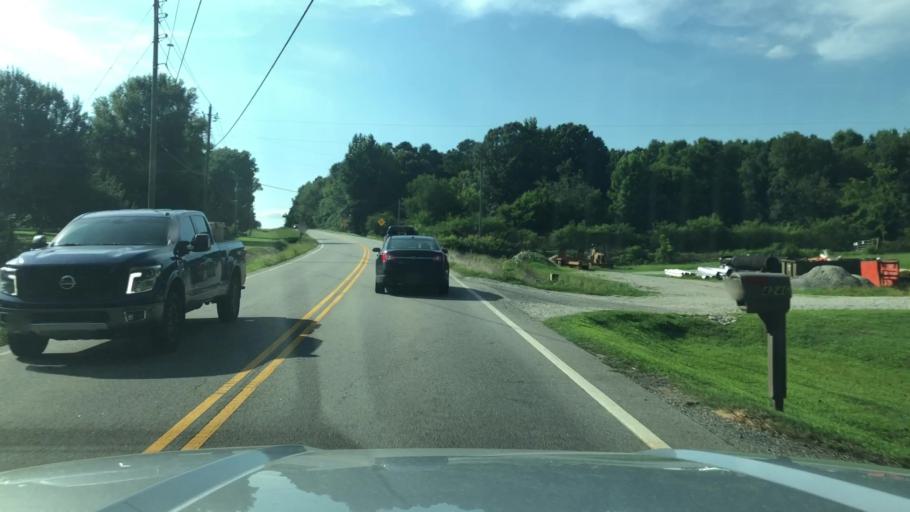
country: US
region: Georgia
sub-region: Paulding County
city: Dallas
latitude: 33.9812
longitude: -84.8657
